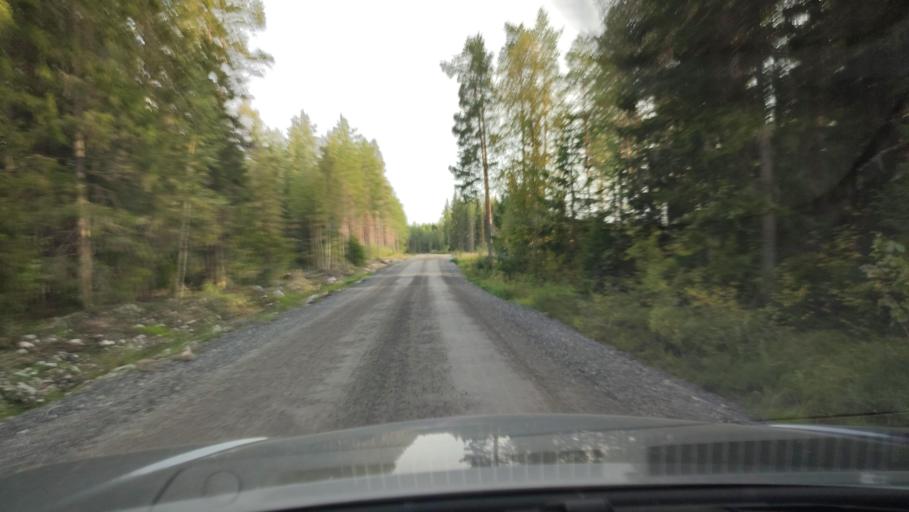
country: FI
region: Southern Ostrobothnia
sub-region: Suupohja
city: Karijoki
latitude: 62.1626
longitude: 21.6100
